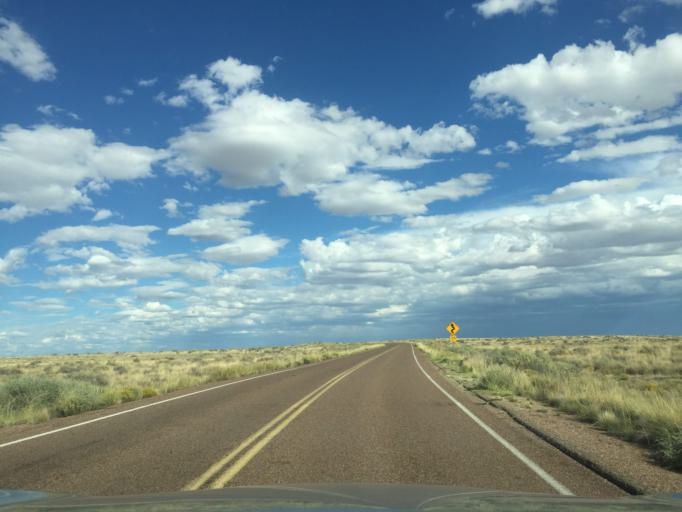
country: US
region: Arizona
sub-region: Navajo County
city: Holbrook
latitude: 34.8924
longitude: -109.7997
